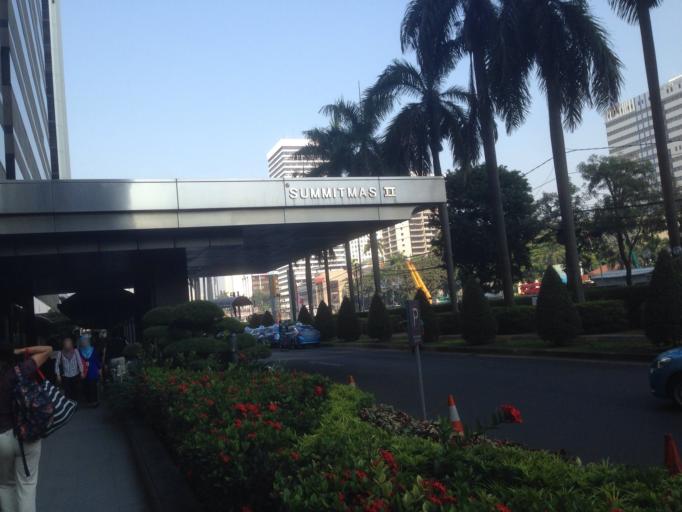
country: ID
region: Jakarta Raya
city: Jakarta
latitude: -6.2260
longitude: 106.8043
